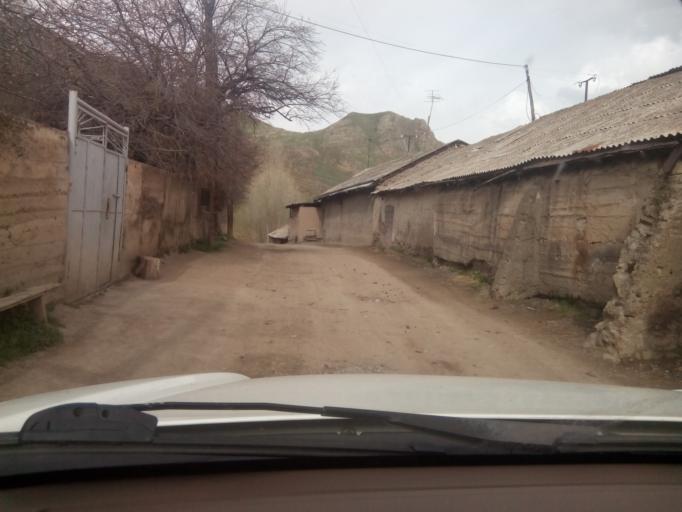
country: AM
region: Syunik'i Marz
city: Hats'avan
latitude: 39.4647
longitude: 45.9247
